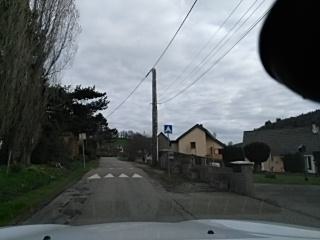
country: FR
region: Alsace
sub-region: Departement du Haut-Rhin
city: Orbey
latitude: 48.1322
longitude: 7.1435
